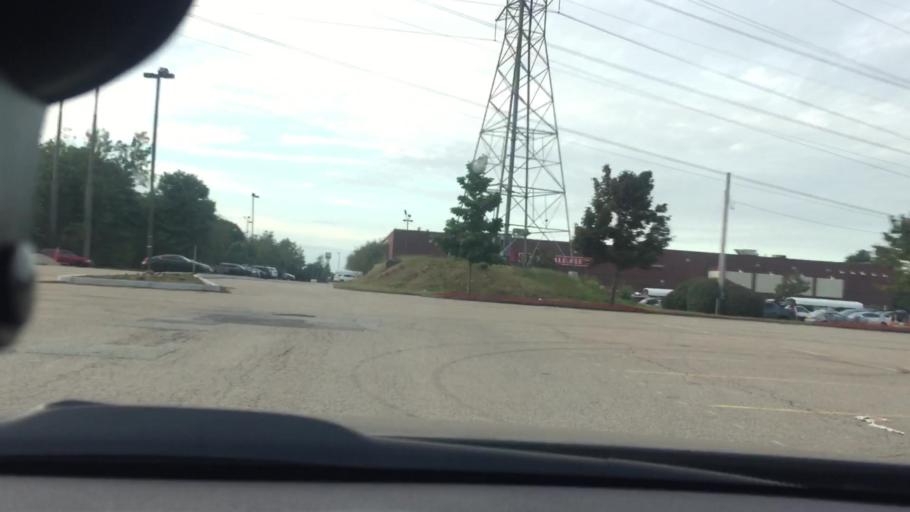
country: US
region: Massachusetts
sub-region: Norfolk County
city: Avon
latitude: 42.1454
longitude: -71.0655
